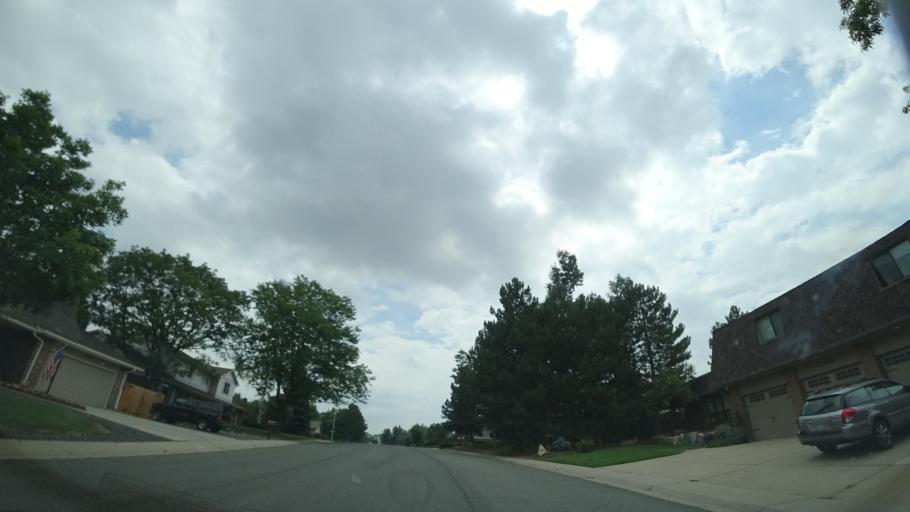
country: US
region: Colorado
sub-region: Jefferson County
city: West Pleasant View
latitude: 39.7121
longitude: -105.1572
